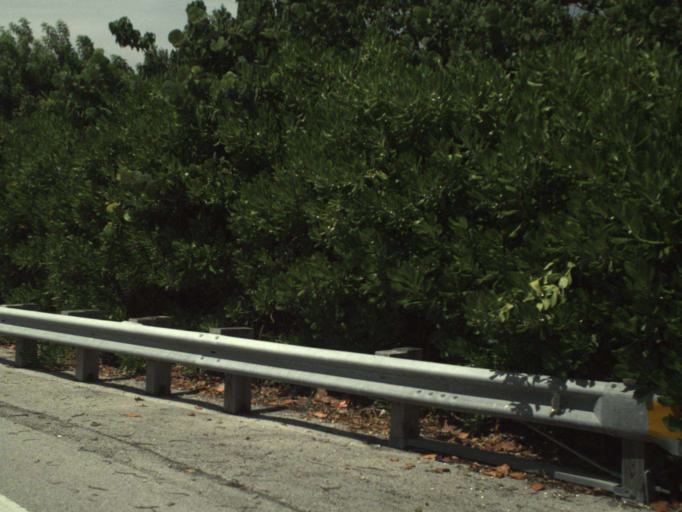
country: US
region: Florida
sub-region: Palm Beach County
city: Hypoluxo
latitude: 26.5618
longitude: -80.0418
